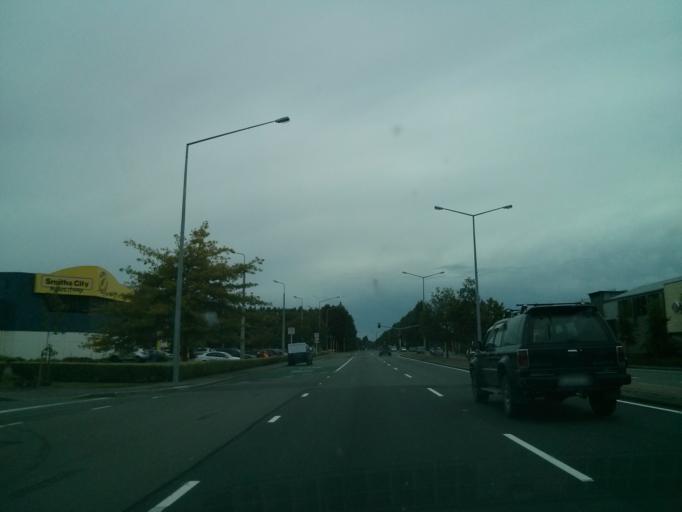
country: NZ
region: Canterbury
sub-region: Christchurch City
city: Christchurch
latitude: -43.4592
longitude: 172.6233
